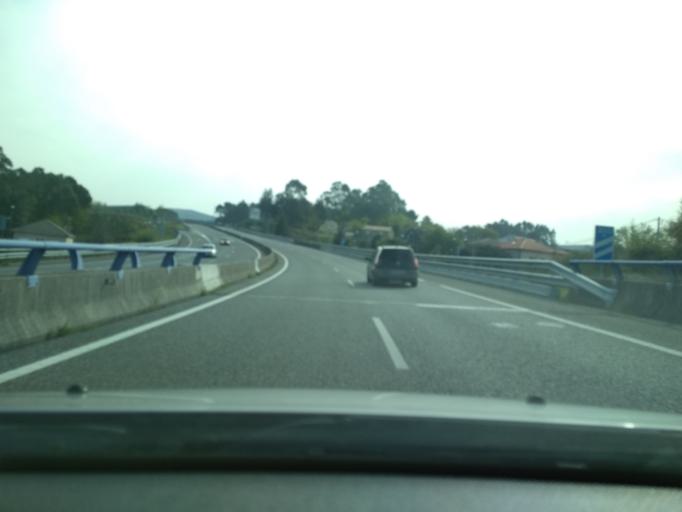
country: ES
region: Galicia
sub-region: Provincia da Coruna
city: Rianxo
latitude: 42.6671
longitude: -8.8120
